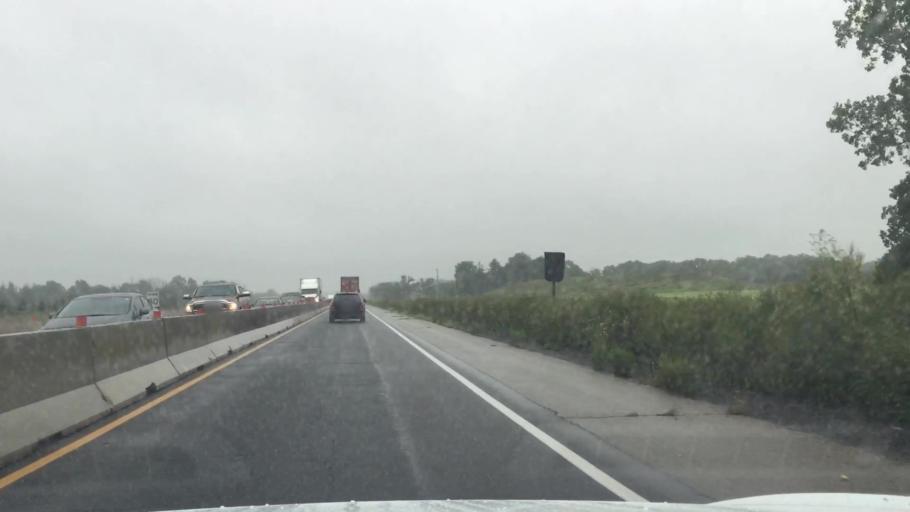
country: CA
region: Ontario
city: Delaware
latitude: 42.8146
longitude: -81.3179
